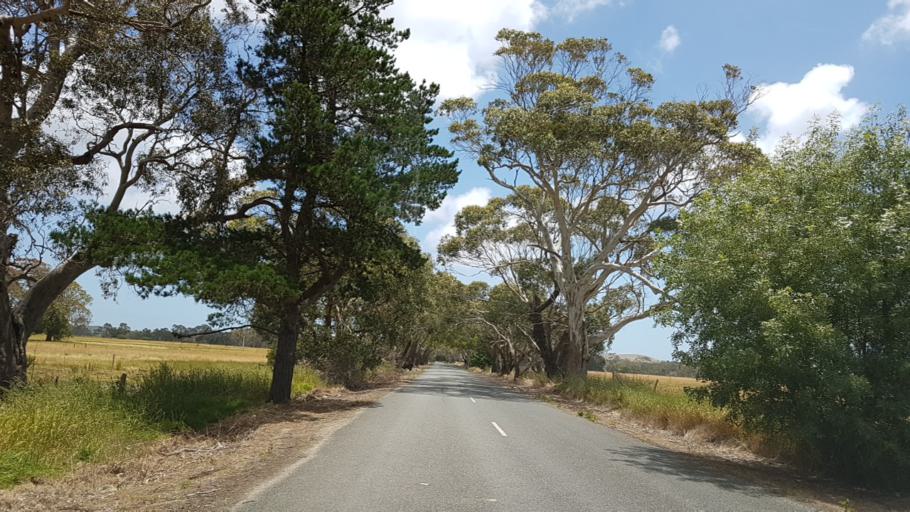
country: AU
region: South Australia
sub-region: Onkaparinga
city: Aldinga
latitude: -35.3772
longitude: 138.4941
